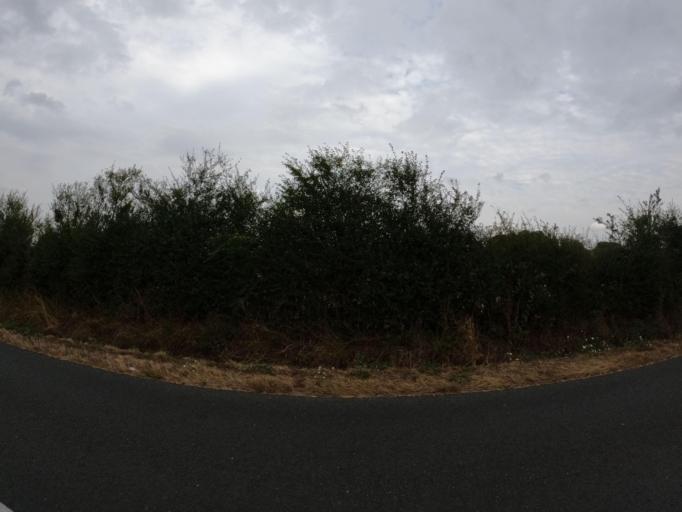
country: FR
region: Pays de la Loire
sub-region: Departement de Maine-et-Loire
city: La Romagne
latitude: 47.0423
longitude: -1.0358
